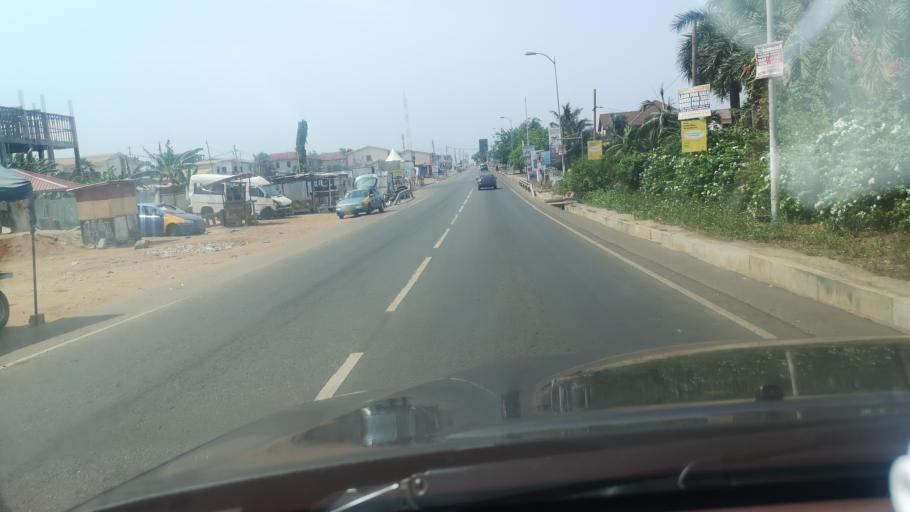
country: GH
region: Greater Accra
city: Nungua
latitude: 5.6440
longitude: -0.0763
